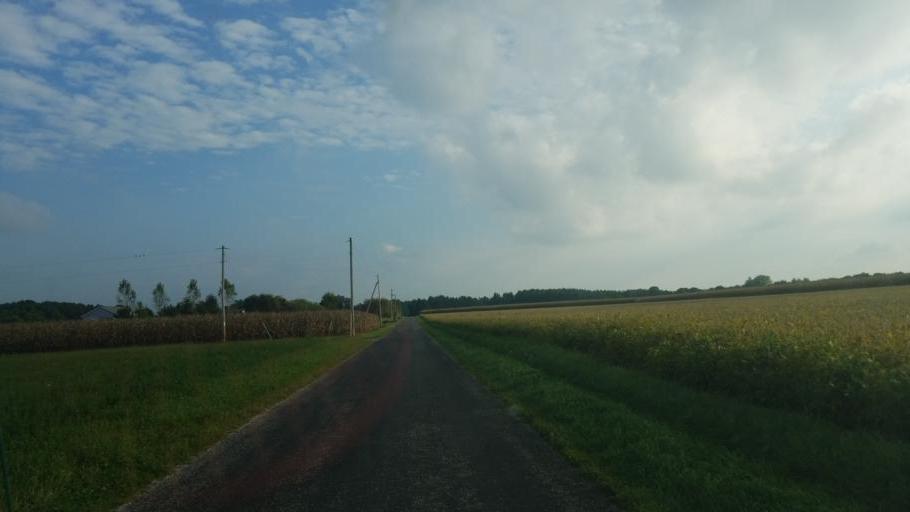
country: US
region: Ohio
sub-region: Wayne County
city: Wooster
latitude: 40.8412
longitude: -82.0336
